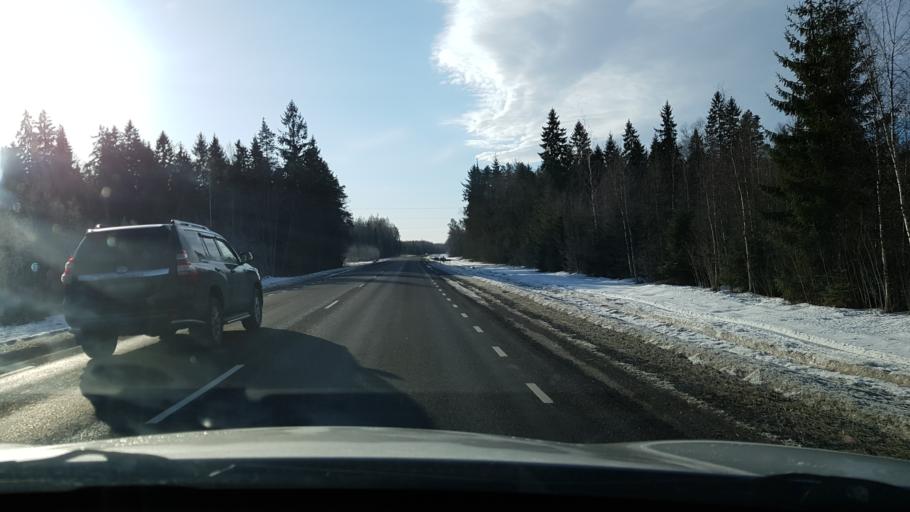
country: EE
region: Viljandimaa
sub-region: Vohma linn
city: Vohma
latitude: 58.6126
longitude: 25.5712
